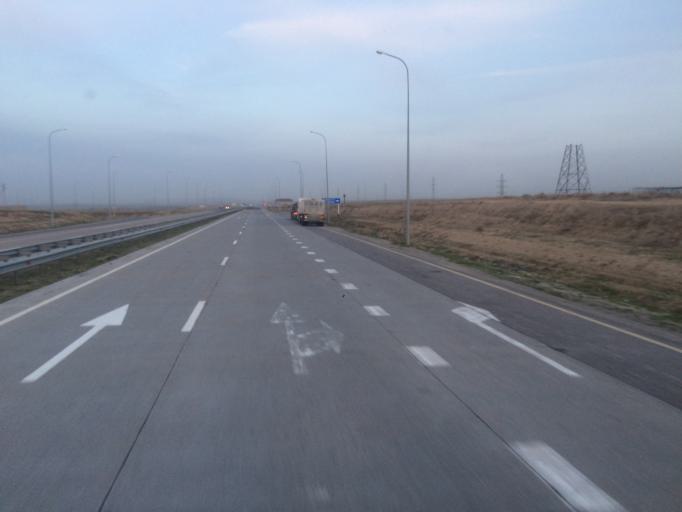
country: KZ
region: Ongtustik Qazaqstan
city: Shymkent
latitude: 42.4525
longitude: 69.6280
